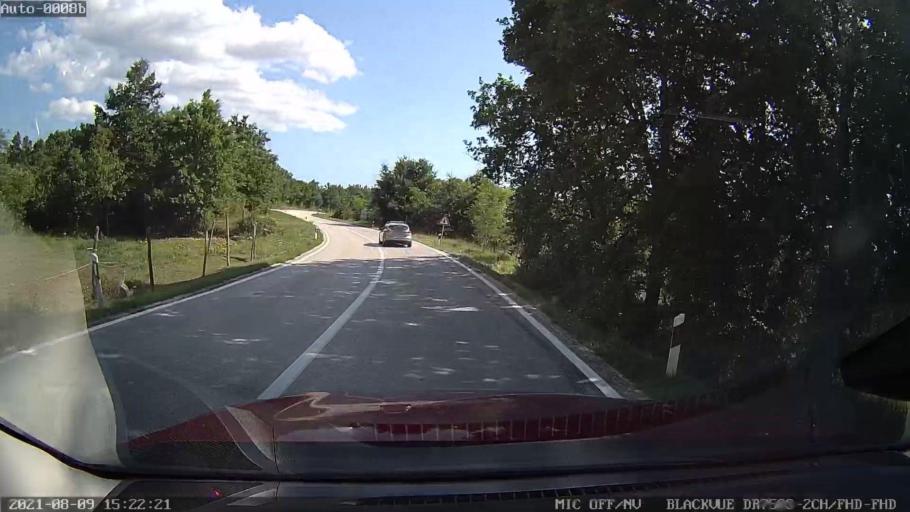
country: HR
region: Istarska
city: Pazin
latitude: 45.1917
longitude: 13.9008
